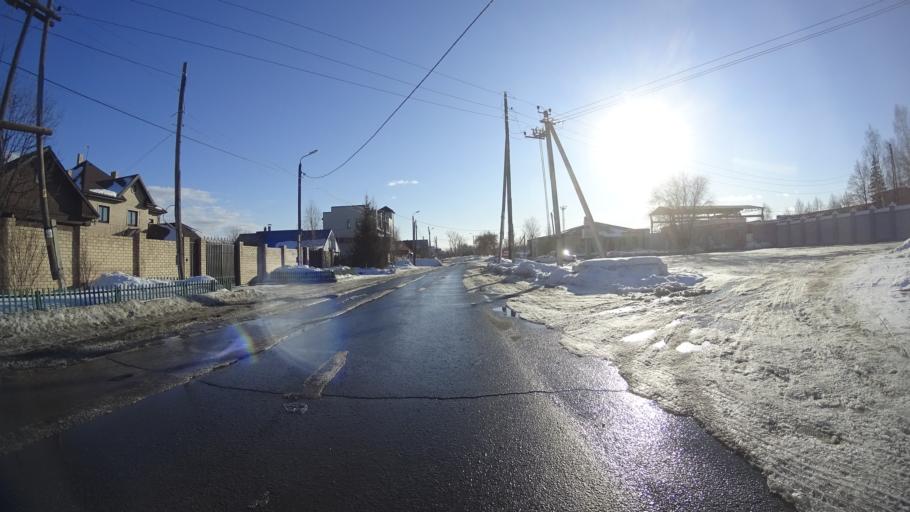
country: RU
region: Chelyabinsk
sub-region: Gorod Chelyabinsk
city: Chelyabinsk
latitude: 55.1509
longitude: 61.3084
